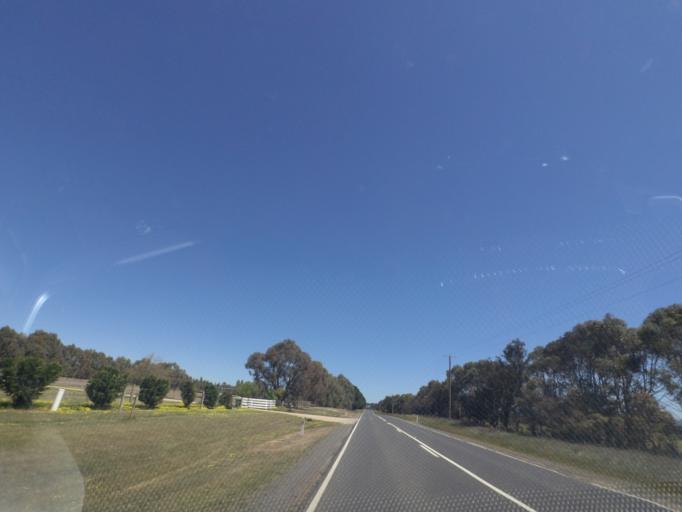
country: AU
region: Victoria
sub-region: Hume
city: Sunbury
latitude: -37.2850
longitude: 144.7679
